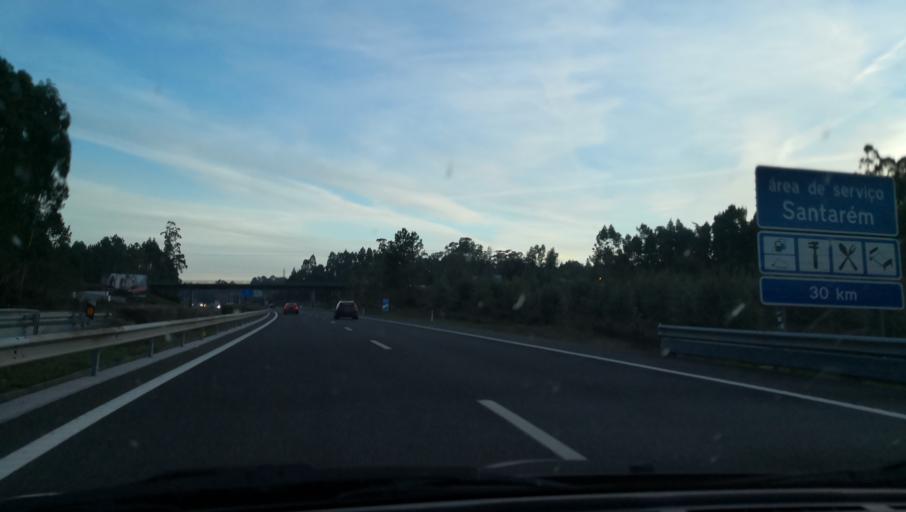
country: PT
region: Santarem
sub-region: Ourem
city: Fatima
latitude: 39.6306
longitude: -8.6984
